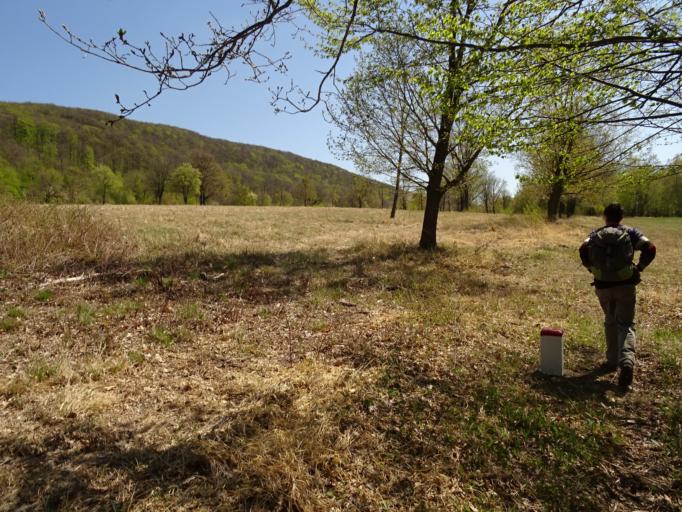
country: HU
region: Borsod-Abauj-Zemplen
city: Gonc
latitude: 48.5675
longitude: 21.4216
